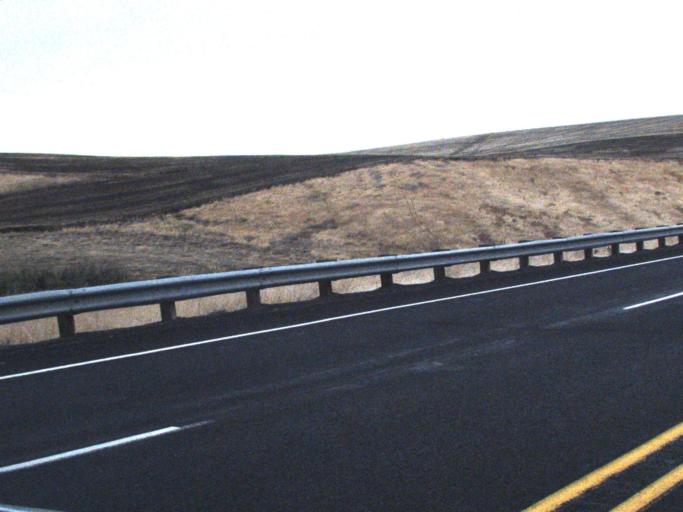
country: US
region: Washington
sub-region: Columbia County
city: Dayton
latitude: 46.4025
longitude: -117.9369
